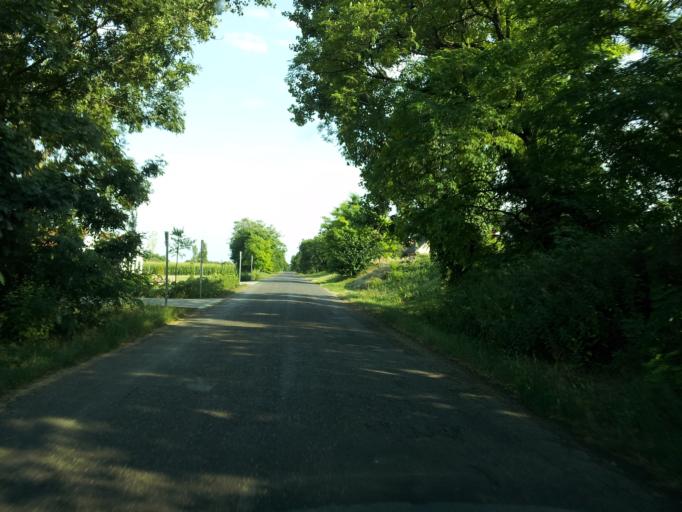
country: HU
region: Fejer
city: Lajoskomarom
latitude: 46.8344
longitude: 18.3422
